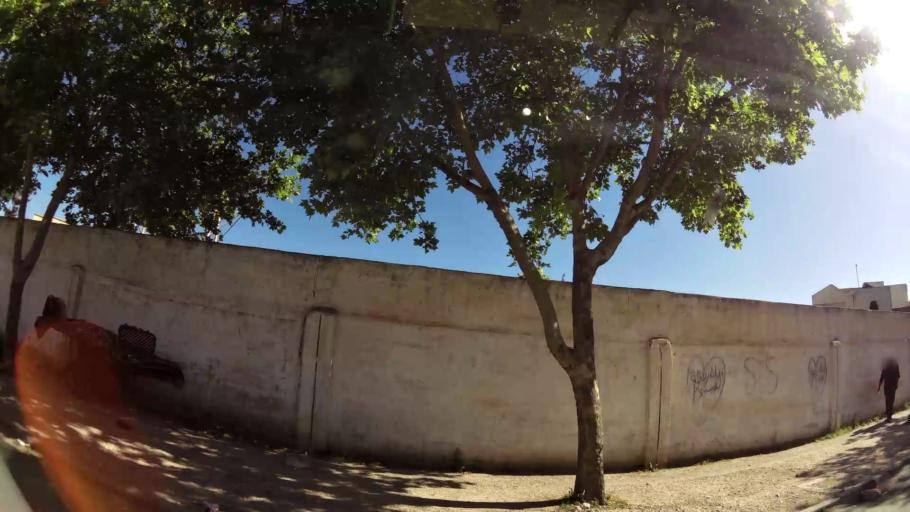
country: MA
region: Fes-Boulemane
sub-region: Fes
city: Fes
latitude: 34.0203
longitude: -4.9766
